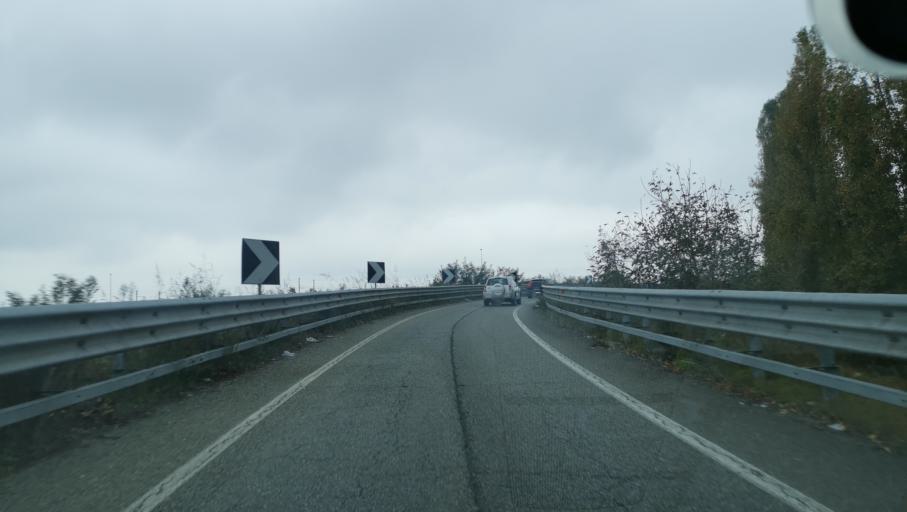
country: IT
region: Piedmont
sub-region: Provincia di Torino
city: Brandizzo
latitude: 45.1698
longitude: 7.8107
